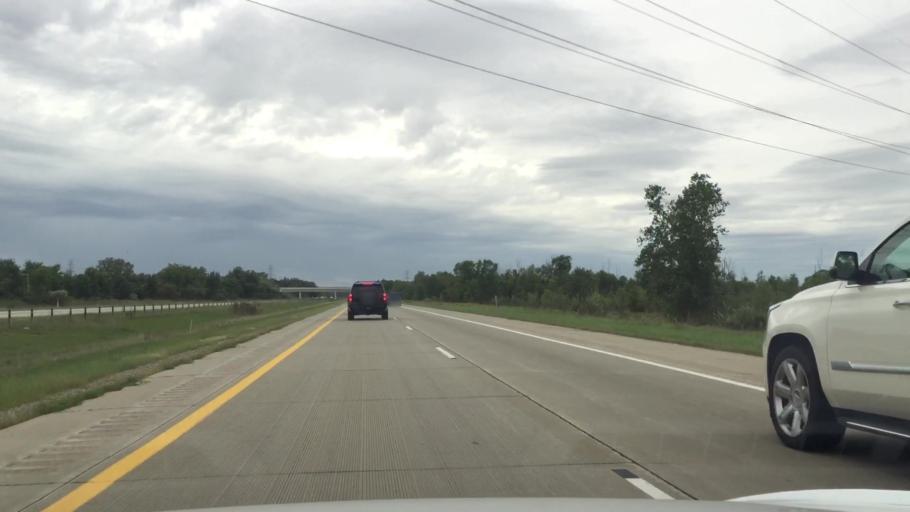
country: US
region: Michigan
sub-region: Macomb County
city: Richmond
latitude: 42.7558
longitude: -82.7046
